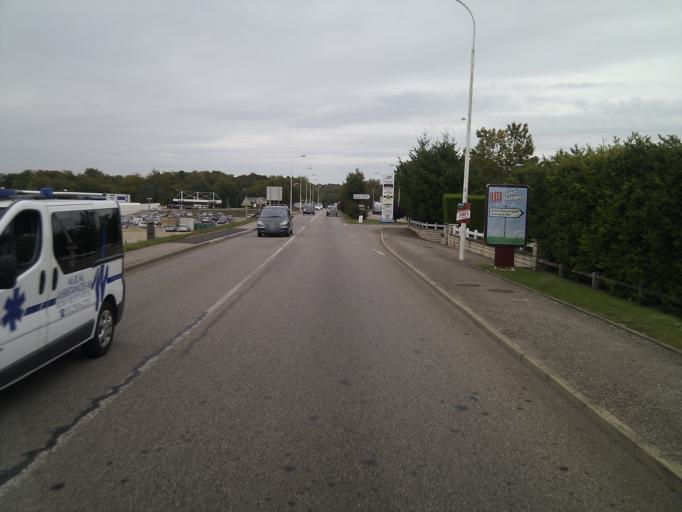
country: FR
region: Lorraine
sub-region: Departement des Vosges
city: Neufchateau
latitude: 48.3683
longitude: 5.7040
